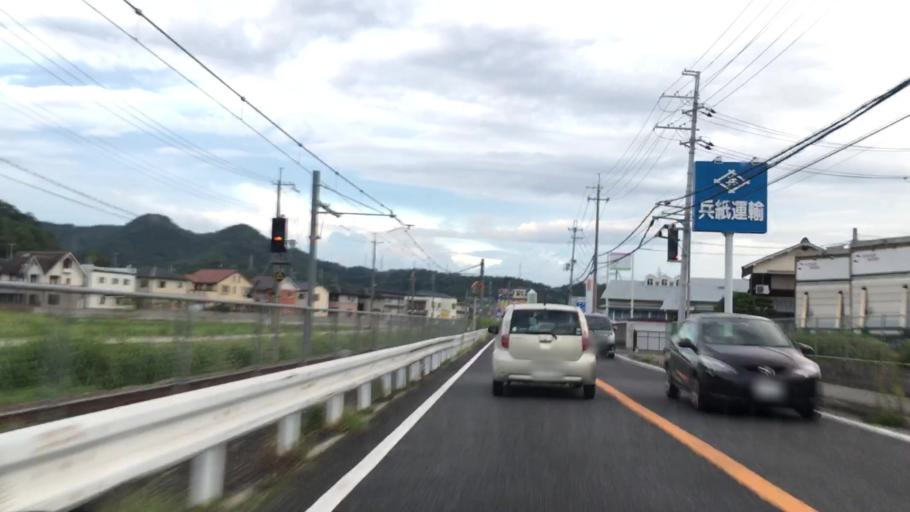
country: JP
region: Hyogo
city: Himeji
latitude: 34.8789
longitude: 134.7289
